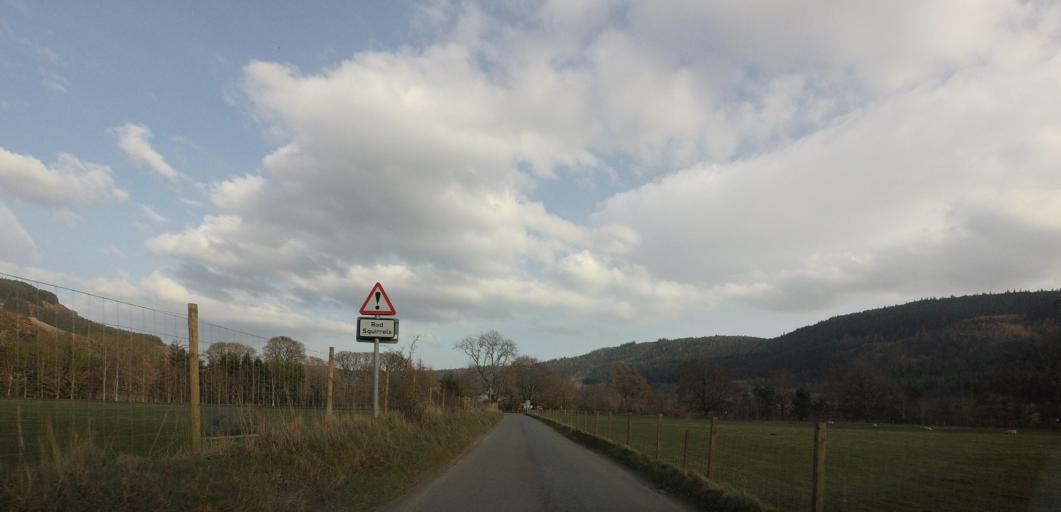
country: GB
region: Scotland
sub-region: Perth and Kinross
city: Aberfeldy
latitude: 56.5969
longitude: -4.0669
